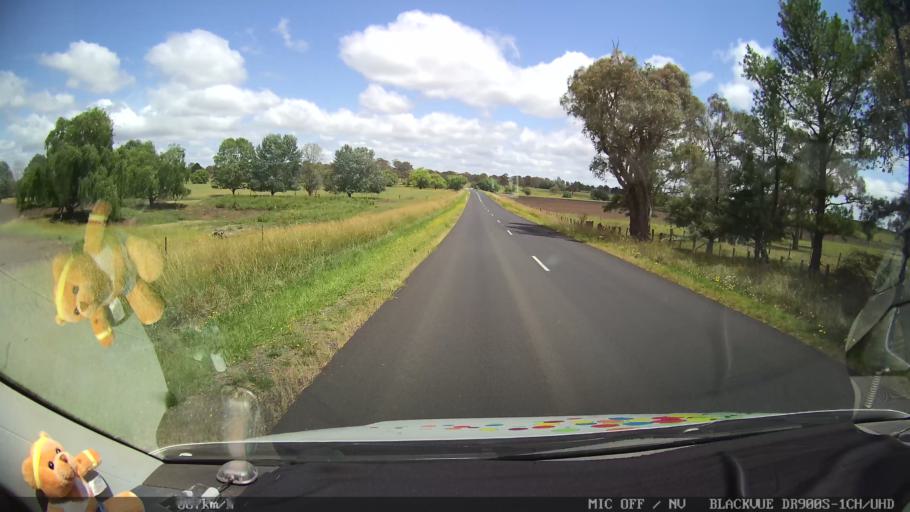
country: AU
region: New South Wales
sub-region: Glen Innes Severn
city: Glen Innes
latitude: -29.6425
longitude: 151.6889
